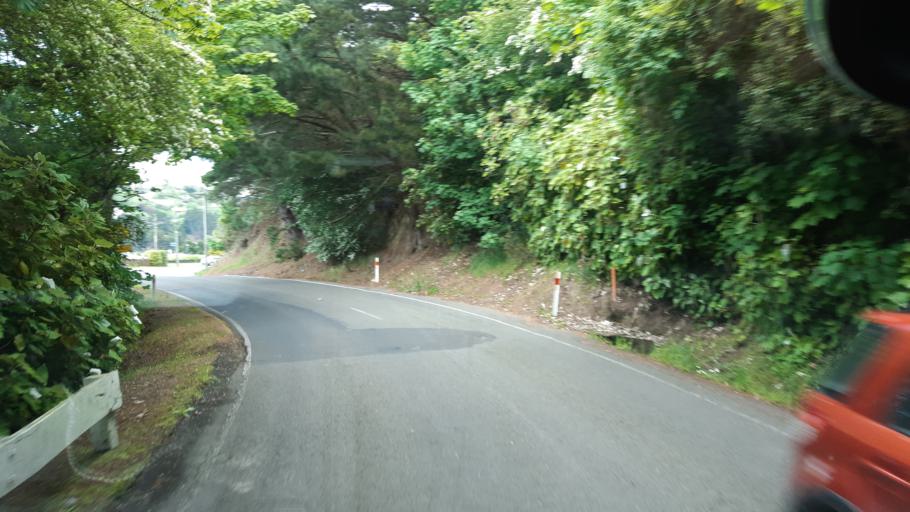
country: NZ
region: Otago
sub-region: Dunedin City
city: Portobello
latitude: -45.8155
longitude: 170.6165
